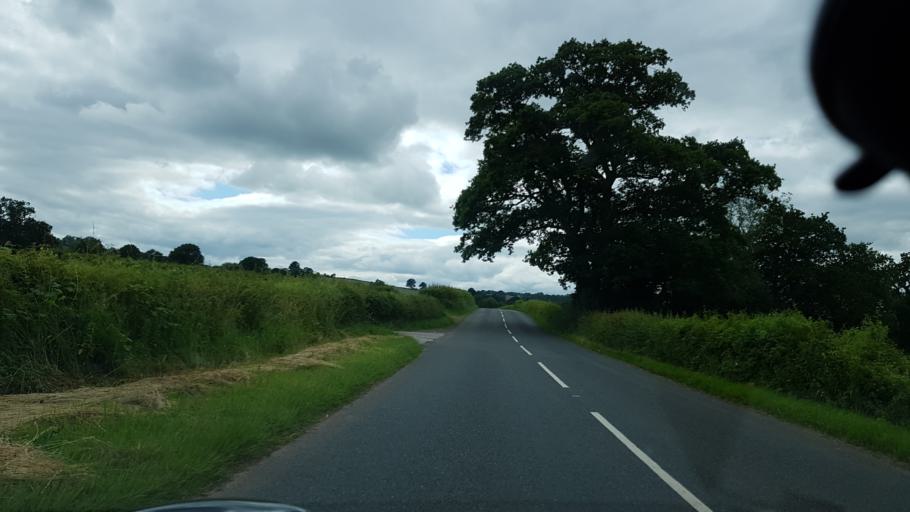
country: GB
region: England
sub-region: Herefordshire
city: Llanrothal
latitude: 51.8778
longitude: -2.7993
